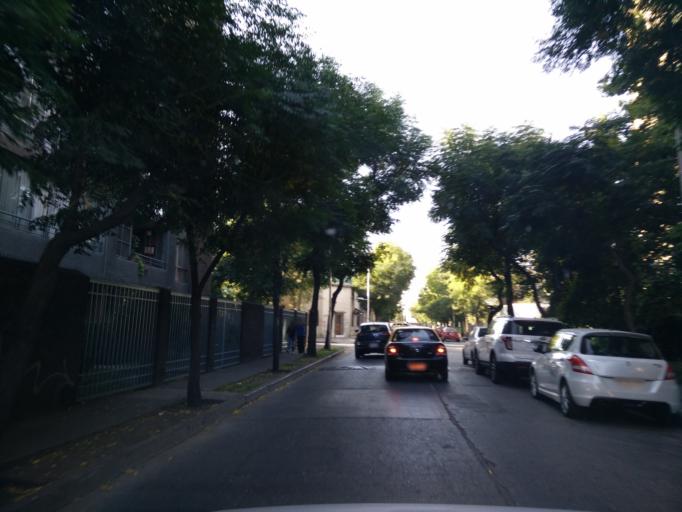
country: CL
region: Santiago Metropolitan
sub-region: Provincia de Santiago
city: Santiago
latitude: -33.4452
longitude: -70.6763
